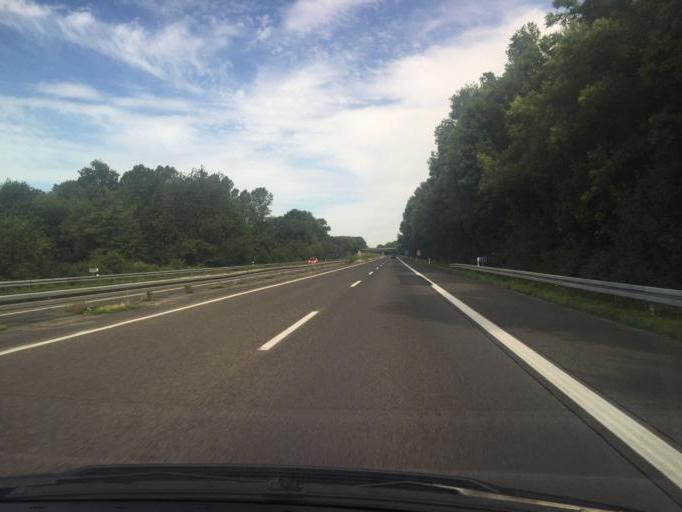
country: DE
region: North Rhine-Westphalia
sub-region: Regierungsbezirk Dusseldorf
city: Sonsbeck
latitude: 51.6079
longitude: 6.3451
